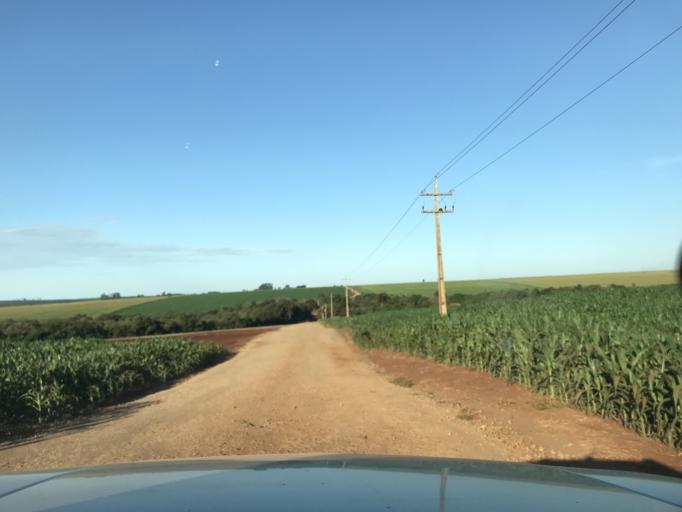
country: BR
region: Parana
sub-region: Palotina
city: Palotina
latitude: -24.2532
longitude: -53.7335
